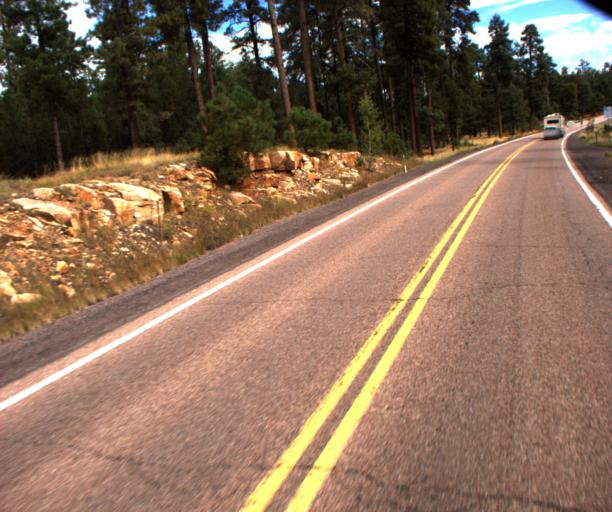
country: US
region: Arizona
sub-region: Navajo County
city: Heber-Overgaard
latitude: 34.3220
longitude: -110.8426
